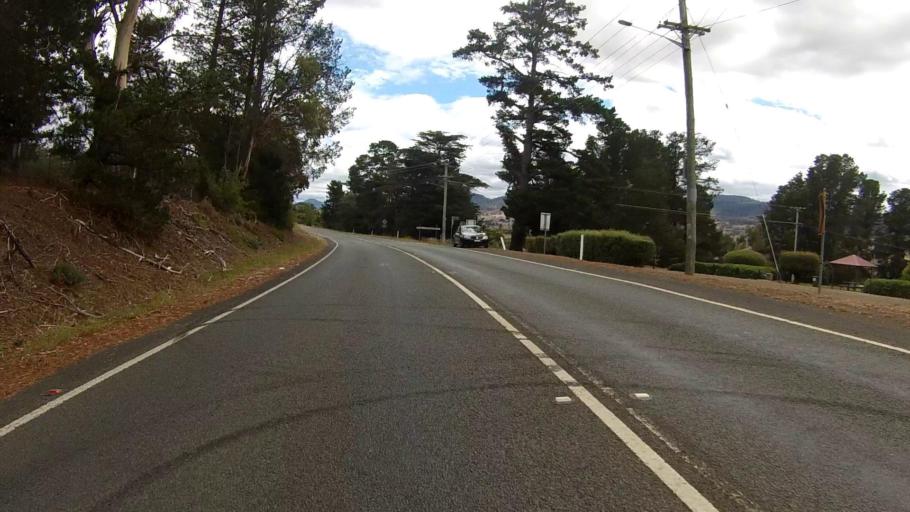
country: AU
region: Tasmania
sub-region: Brighton
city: Bridgewater
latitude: -42.6803
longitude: 147.2659
